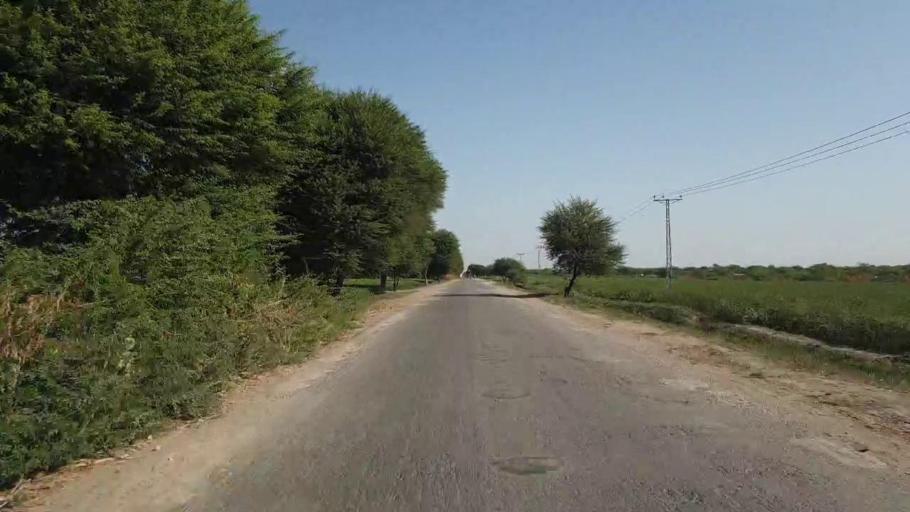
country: PK
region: Sindh
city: Umarkot
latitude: 25.4354
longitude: 69.7459
